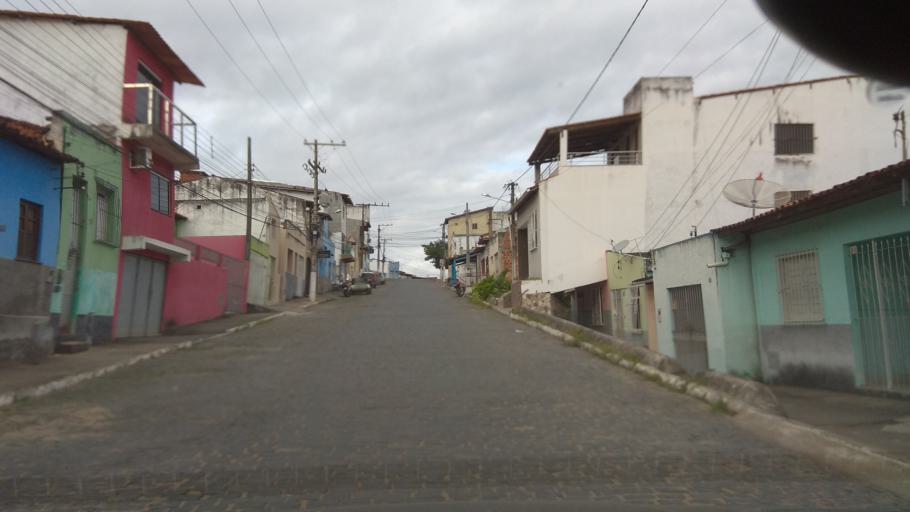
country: BR
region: Bahia
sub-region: Ipiau
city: Ipiau
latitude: -14.1369
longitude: -39.7382
